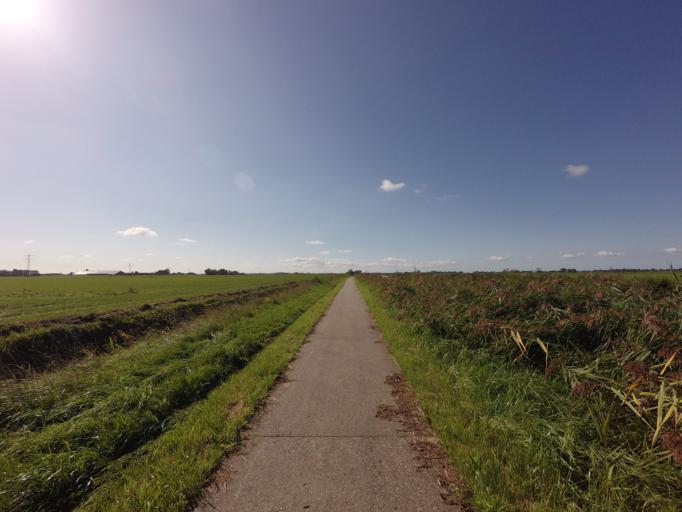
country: NL
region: Friesland
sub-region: Gemeente Boarnsterhim
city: Reduzum
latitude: 53.1402
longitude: 5.7627
